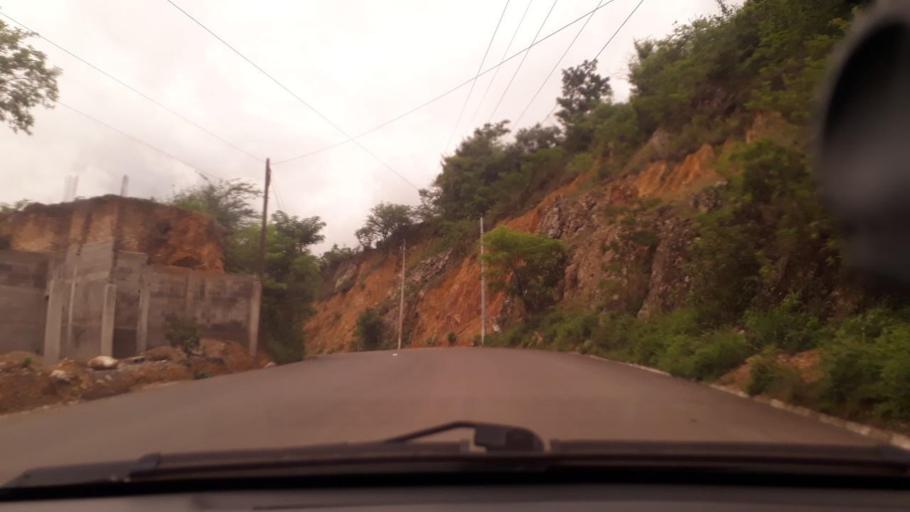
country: GT
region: Chiquimula
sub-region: Municipio de San Juan Ermita
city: San Juan Ermita
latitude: 14.7459
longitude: -89.4604
